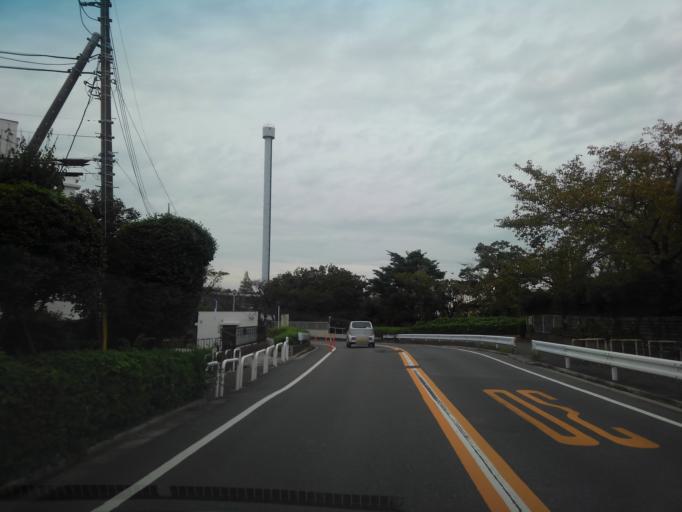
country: JP
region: Tokyo
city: Higashimurayama-shi
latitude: 35.7668
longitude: 139.4433
